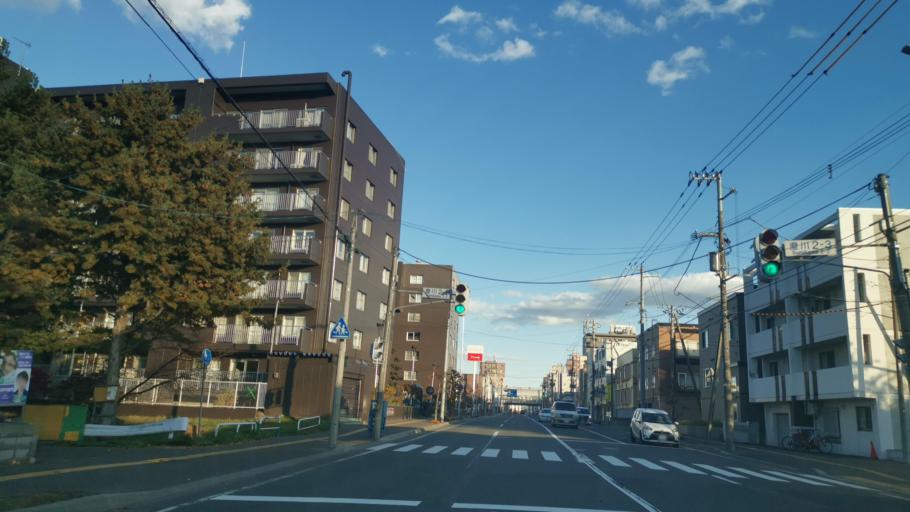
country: JP
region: Hokkaido
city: Sapporo
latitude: 43.0159
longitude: 141.3625
